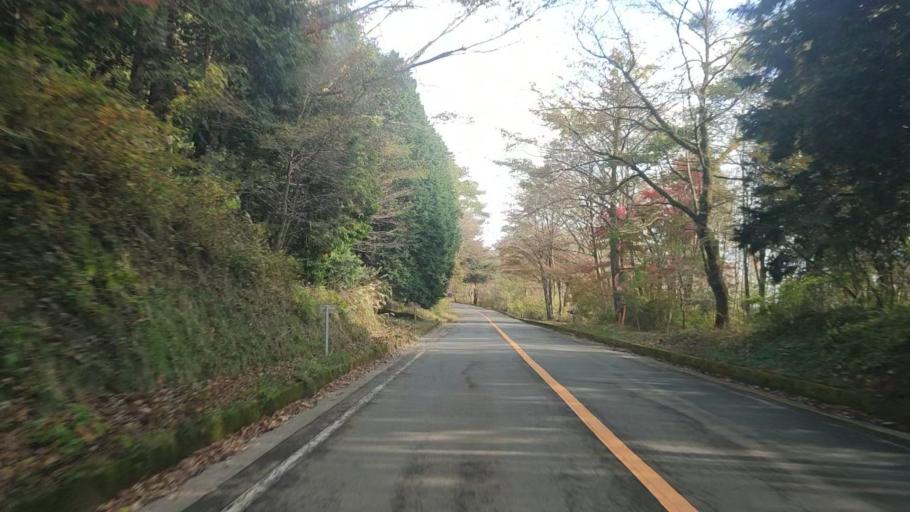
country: JP
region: Shizuoka
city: Fujinomiya
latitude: 35.3008
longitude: 138.6857
